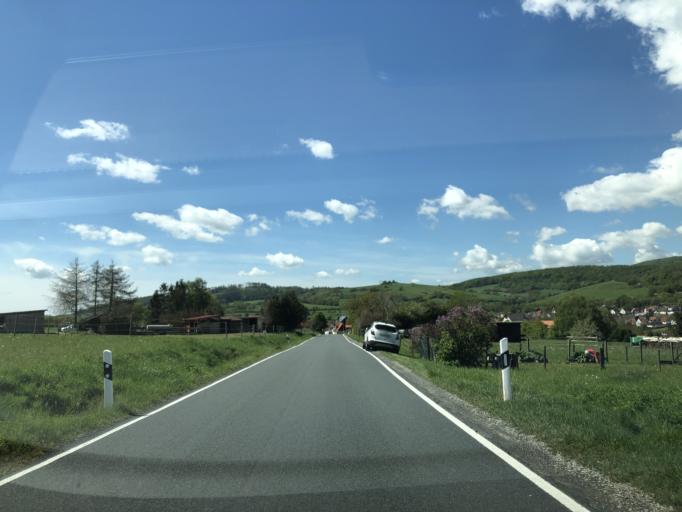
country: DE
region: Hesse
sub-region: Regierungsbezirk Kassel
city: Grossalmerode
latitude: 51.2327
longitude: 9.8218
